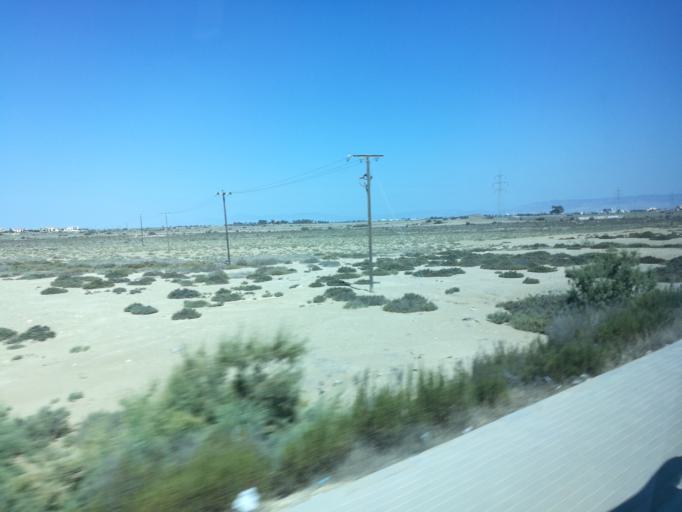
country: CY
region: Ammochostos
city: Famagusta
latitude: 35.1670
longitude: 33.8989
